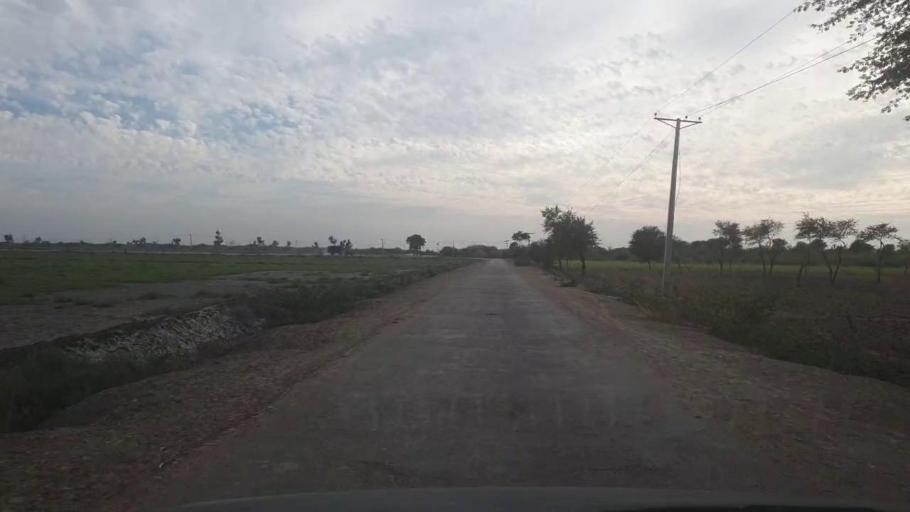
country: PK
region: Sindh
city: Samaro
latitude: 25.3250
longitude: 69.2358
